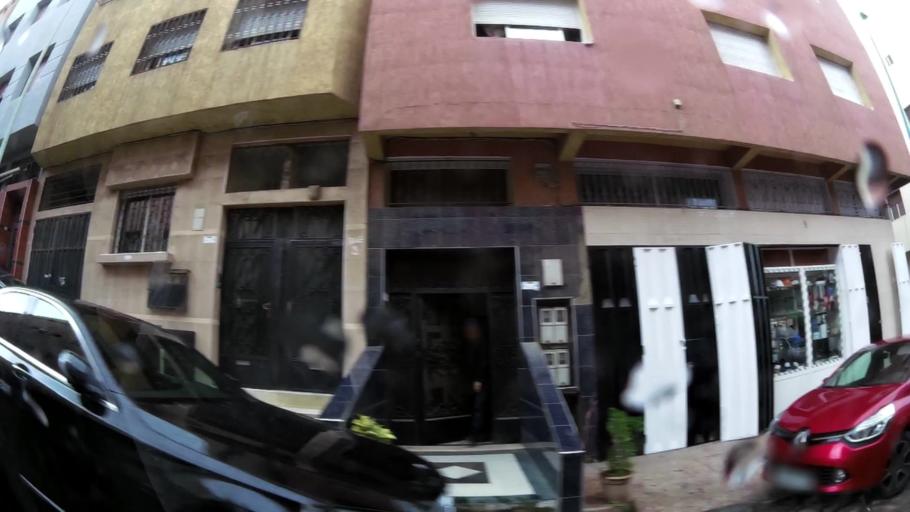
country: MA
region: Grand Casablanca
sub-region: Mediouna
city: Tit Mellil
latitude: 33.6194
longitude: -7.4858
